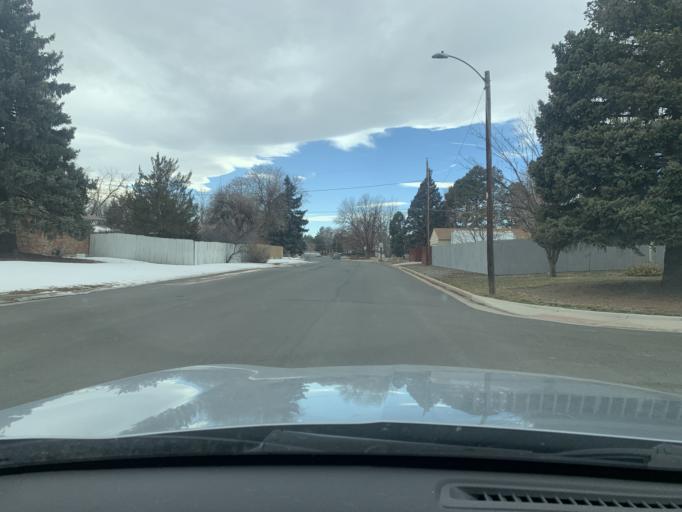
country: US
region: Colorado
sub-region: Arapahoe County
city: Glendale
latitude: 39.6582
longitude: -104.8723
